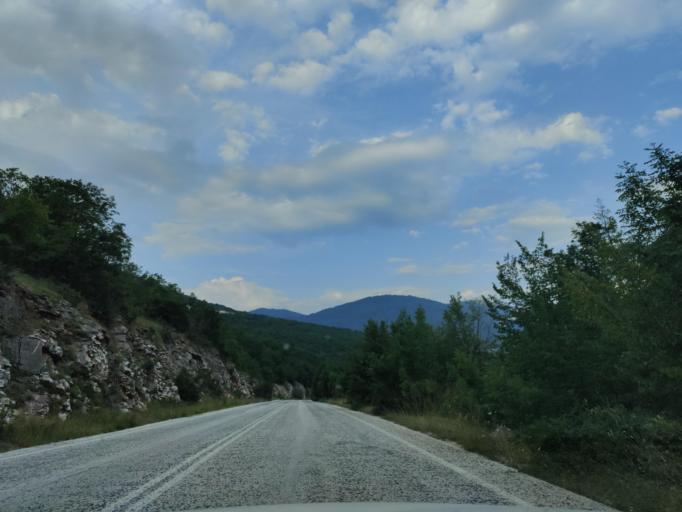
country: GR
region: East Macedonia and Thrace
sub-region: Nomos Dramas
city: Volakas
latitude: 41.2919
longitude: 23.9578
